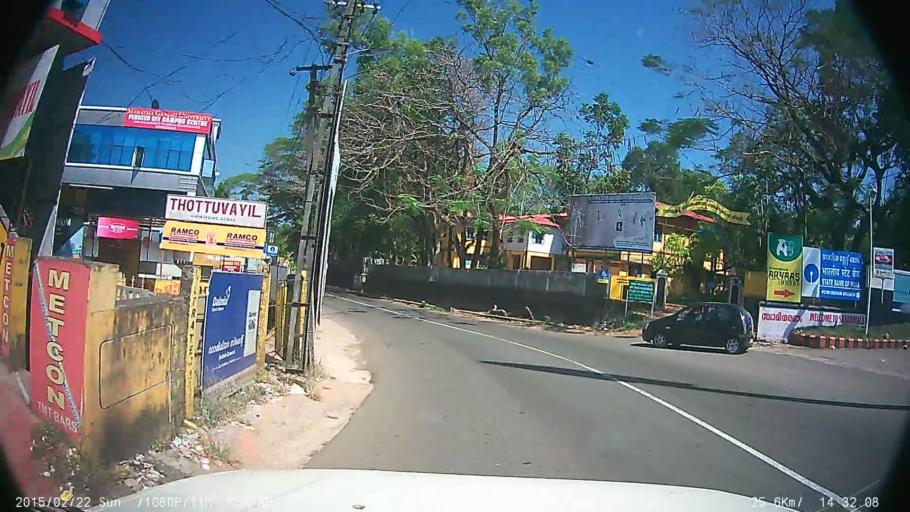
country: IN
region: Kerala
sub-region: Kottayam
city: Erattupetta
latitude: 9.5634
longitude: 76.7593
